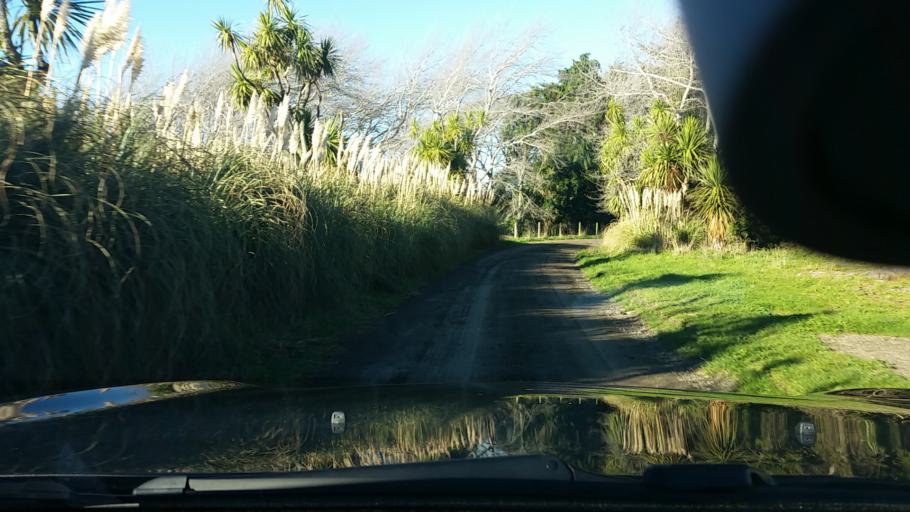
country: NZ
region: Marlborough
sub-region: Marlborough District
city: Blenheim
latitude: -41.6383
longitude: 174.0215
